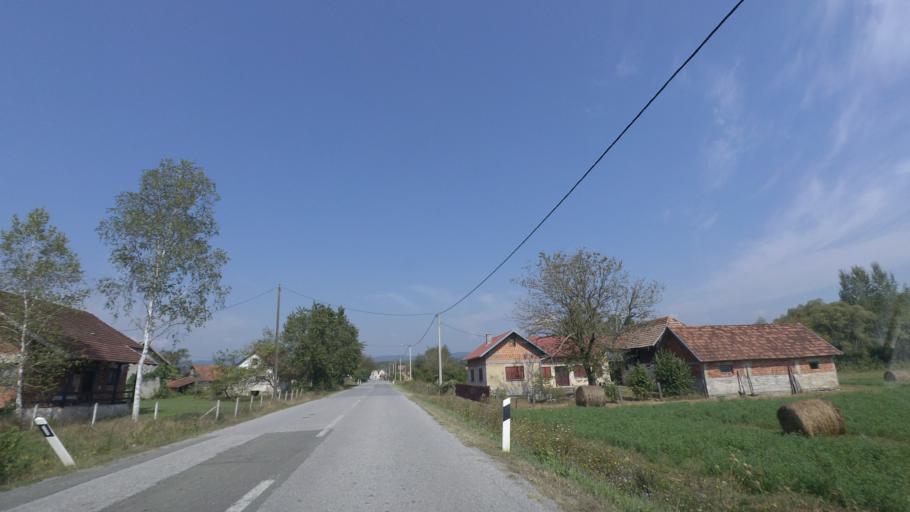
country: HR
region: Sisacko-Moslavacka
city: Dvor
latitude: 45.1124
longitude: 16.2775
